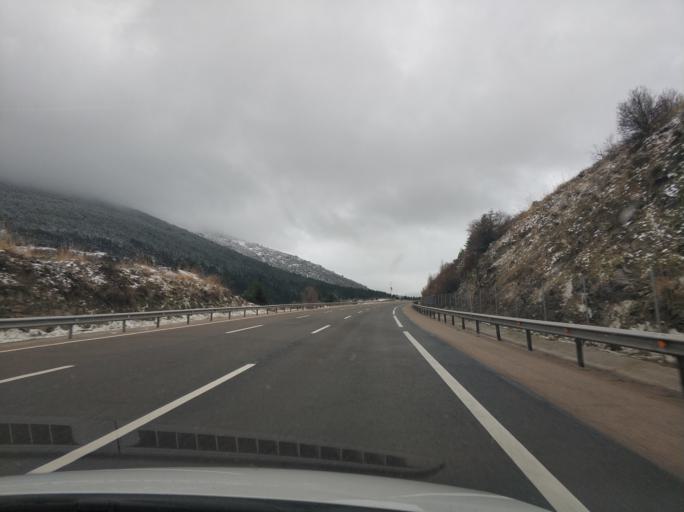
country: ES
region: Madrid
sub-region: Provincia de Madrid
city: Somosierra
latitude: 41.1717
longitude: -3.5824
